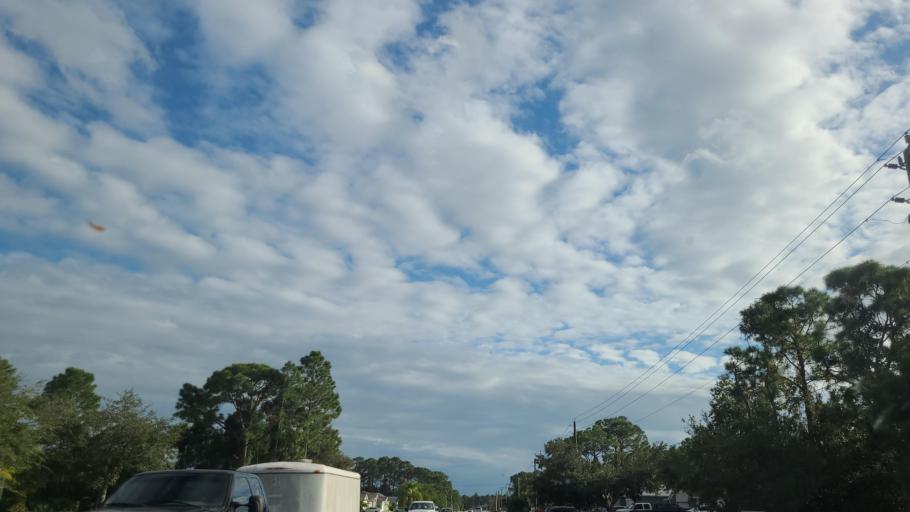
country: US
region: Florida
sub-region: Brevard County
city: June Park
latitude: 28.0024
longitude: -80.6970
